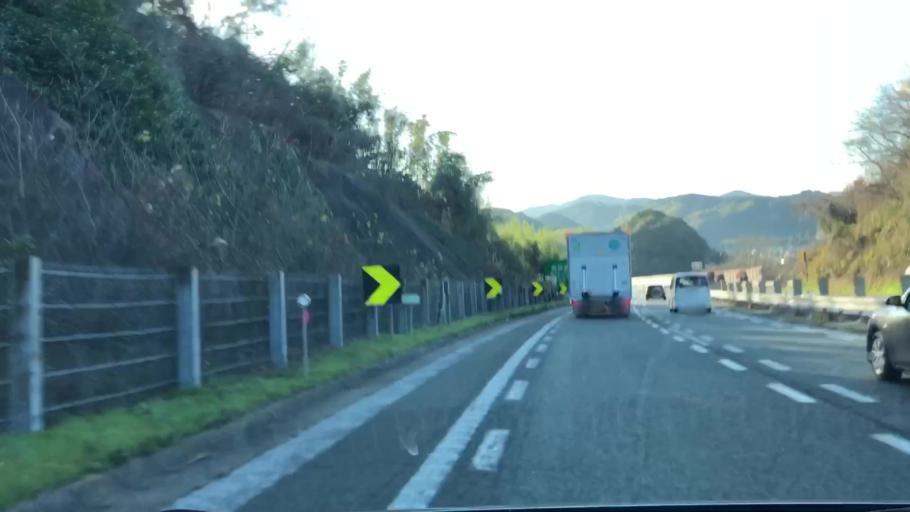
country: JP
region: Yamaguchi
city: Onoda
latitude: 34.1100
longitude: 131.1547
